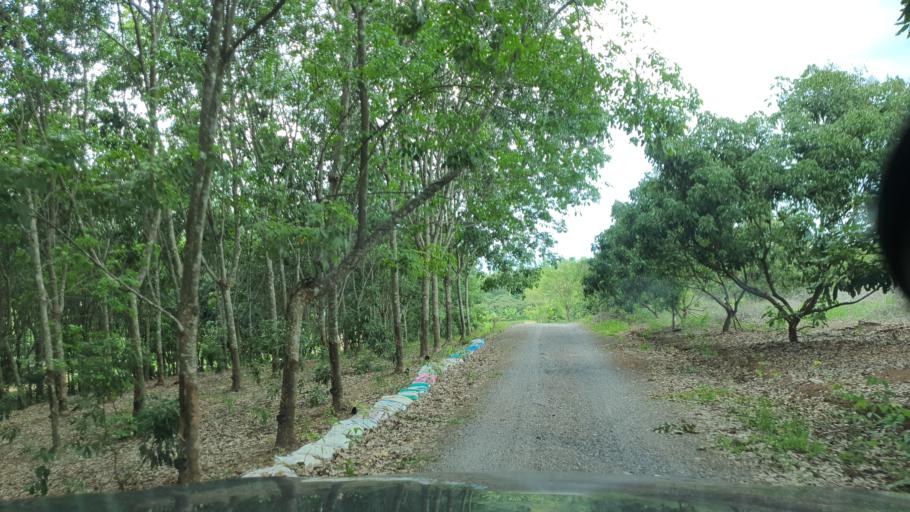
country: TH
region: Chiang Mai
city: Mae Taeng
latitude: 19.1278
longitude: 99.0452
